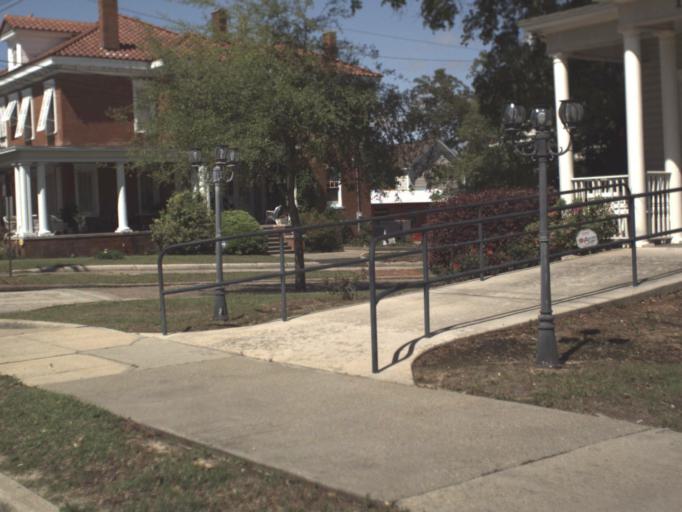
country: US
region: Florida
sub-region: Escambia County
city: Pensacola
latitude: 30.4249
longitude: -87.2181
